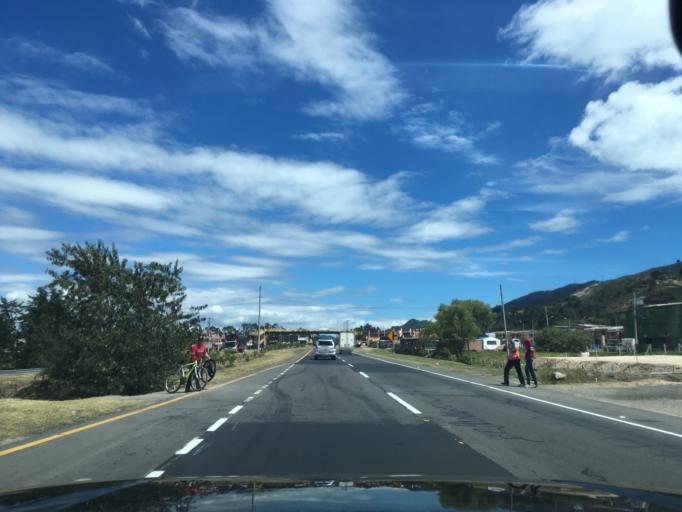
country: CO
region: Cundinamarca
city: Tocancipa
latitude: 4.9645
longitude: -73.9079
